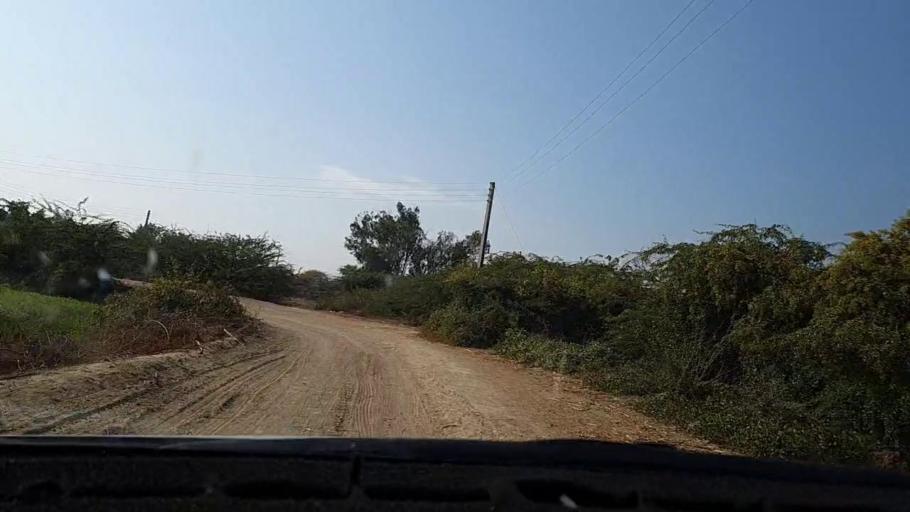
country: PK
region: Sindh
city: Tando Mittha Khan
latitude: 25.8123
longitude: 69.2967
